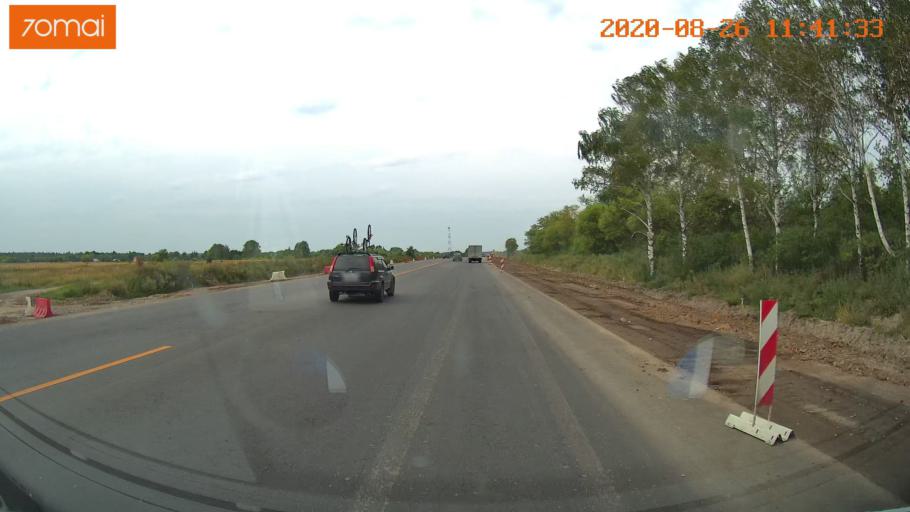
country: RU
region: Rjazan
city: Shilovo
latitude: 54.2955
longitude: 40.7092
